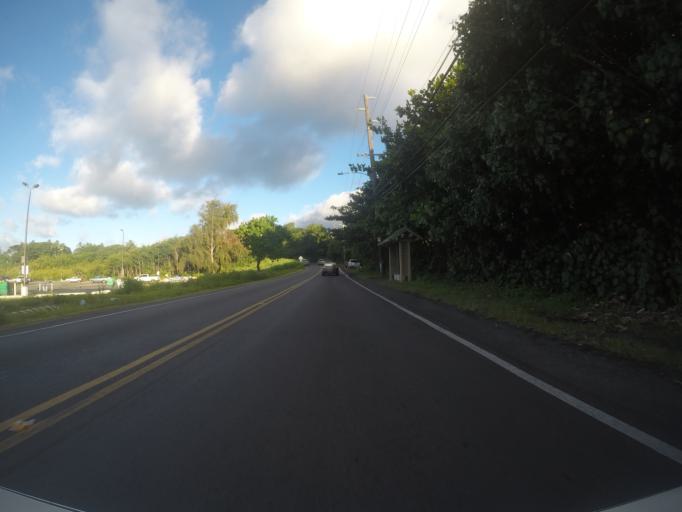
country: US
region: Hawaii
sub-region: Honolulu County
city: He'eia
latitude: 21.4425
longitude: -157.8116
